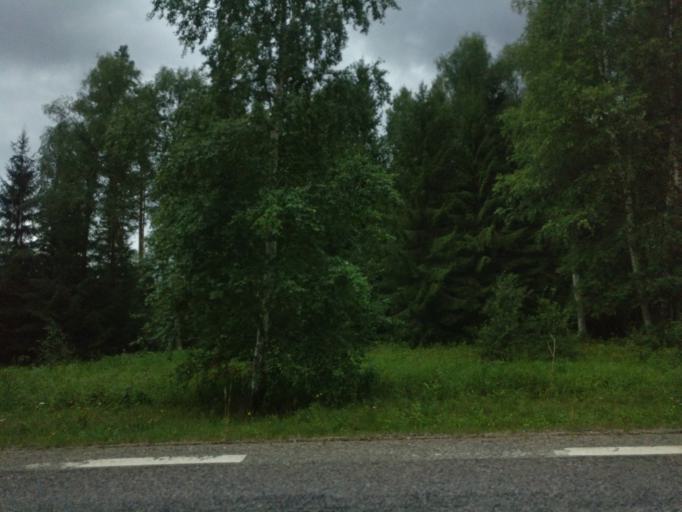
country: SE
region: Vaermland
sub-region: Torsby Kommun
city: Torsby
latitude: 60.7732
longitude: 12.7516
